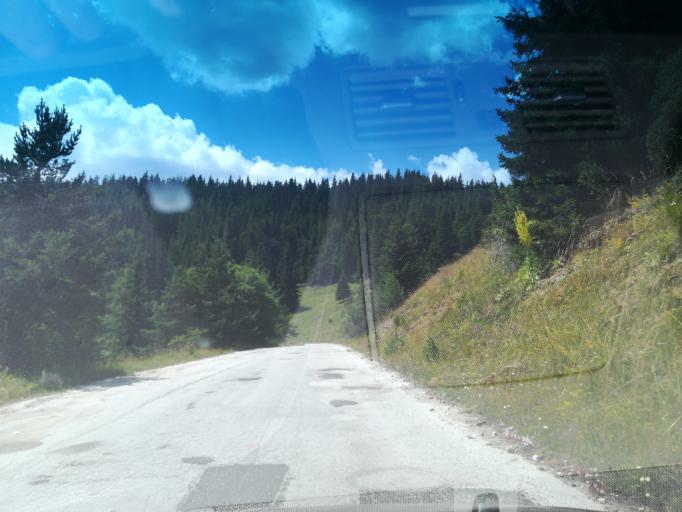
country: BG
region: Smolyan
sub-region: Obshtina Chepelare
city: Chepelare
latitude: 41.6925
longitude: 24.7577
